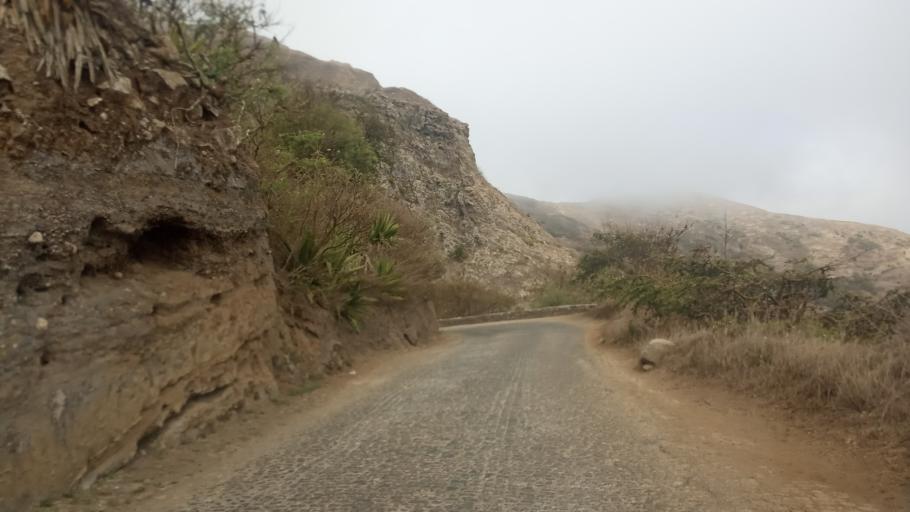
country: CV
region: Brava
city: Vila Nova Sintra
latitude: 14.8674
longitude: -24.7070
